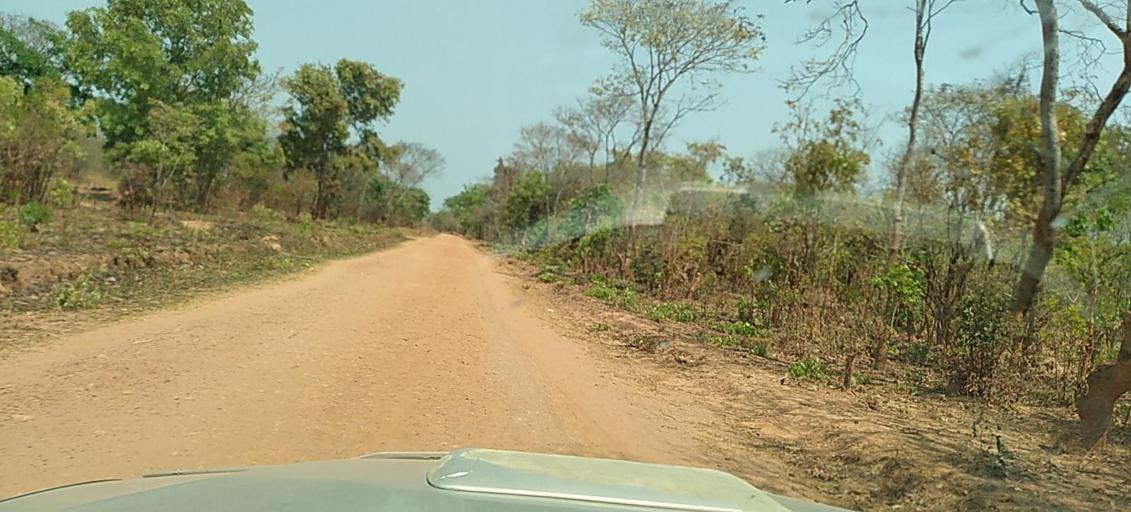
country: ZM
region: North-Western
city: Kasempa
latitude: -13.7010
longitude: 26.3311
